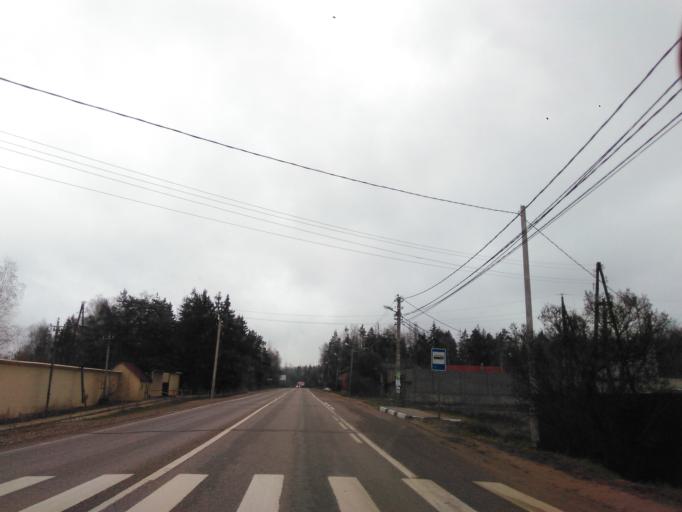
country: RU
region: Moskovskaya
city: Rozhdestveno
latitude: 55.8366
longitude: 37.0142
